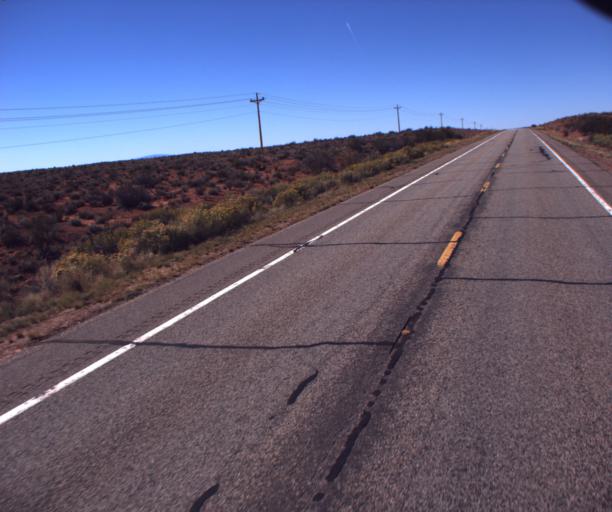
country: US
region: Arizona
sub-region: Coconino County
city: Fredonia
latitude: 36.8731
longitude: -112.6718
